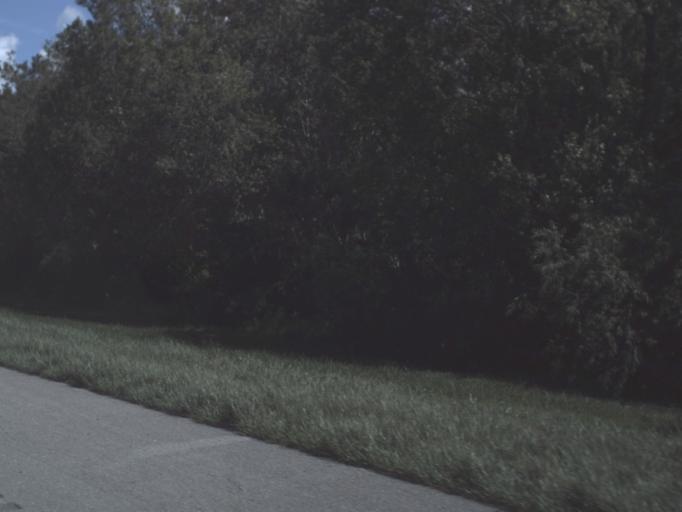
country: US
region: Florida
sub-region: Sarasota County
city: Vamo
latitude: 27.2368
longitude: -82.4518
